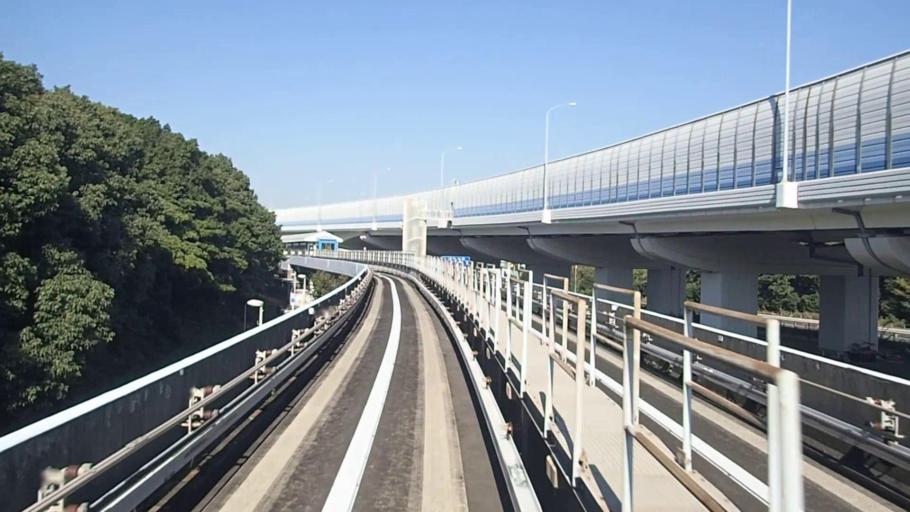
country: JP
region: Kanagawa
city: Yokohama
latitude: 35.3758
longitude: 139.6424
